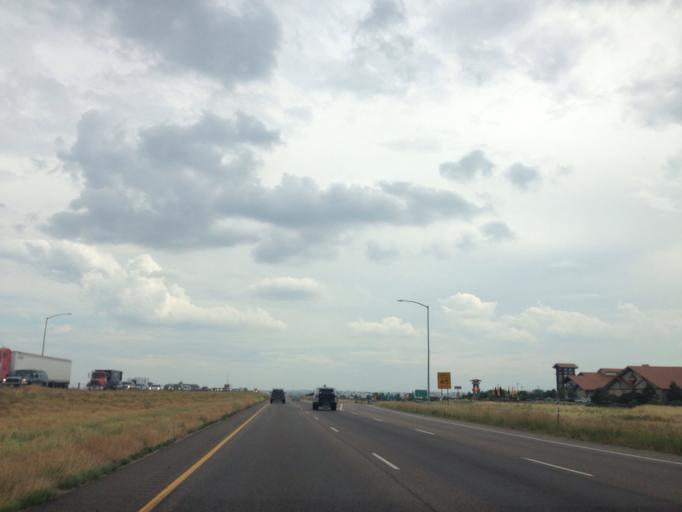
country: US
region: Colorado
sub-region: Larimer County
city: Loveland
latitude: 40.4403
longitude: -104.9924
